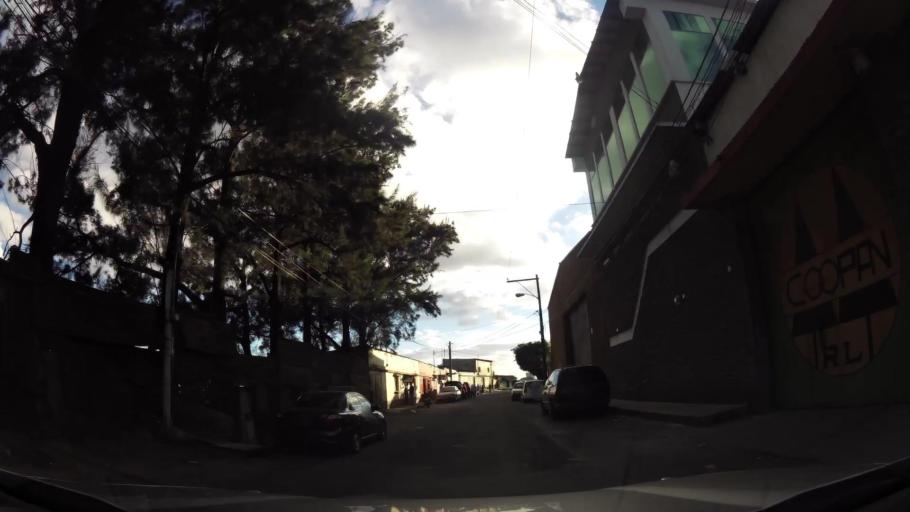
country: GT
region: Guatemala
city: Guatemala City
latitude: 14.6230
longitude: -90.5195
